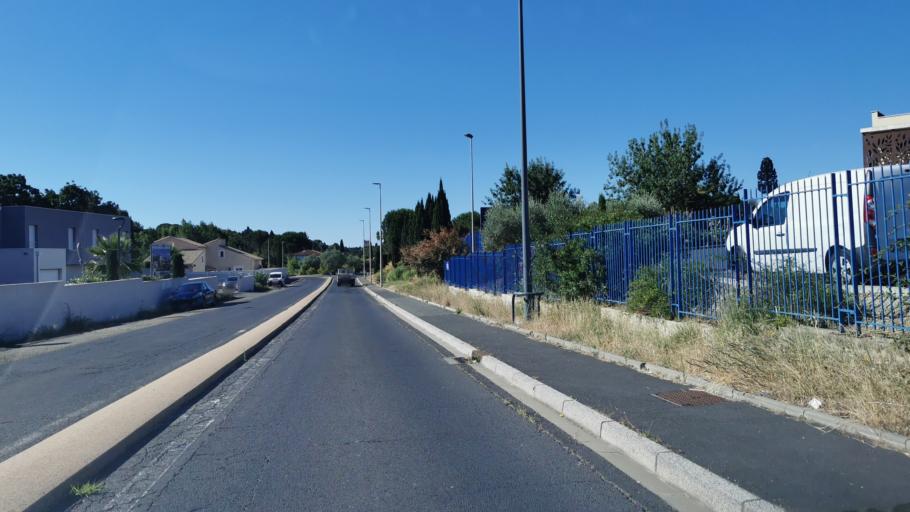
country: FR
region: Languedoc-Roussillon
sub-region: Departement de l'Herault
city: Beziers
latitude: 43.3624
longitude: 3.2121
